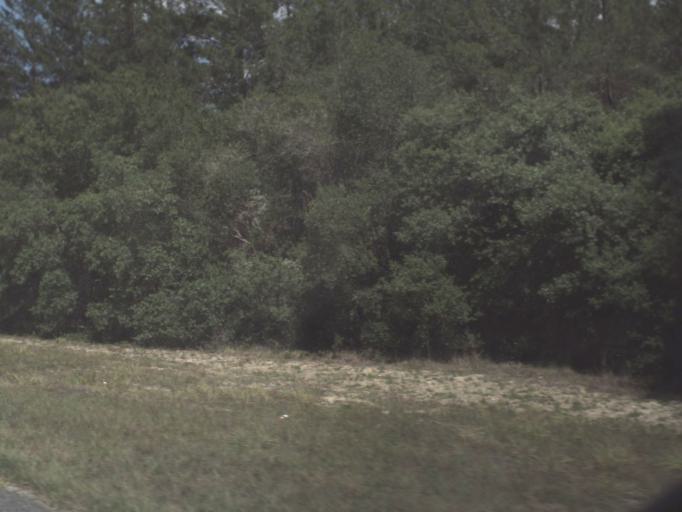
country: US
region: Florida
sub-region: Lake County
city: Astor
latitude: 29.1777
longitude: -81.7453
